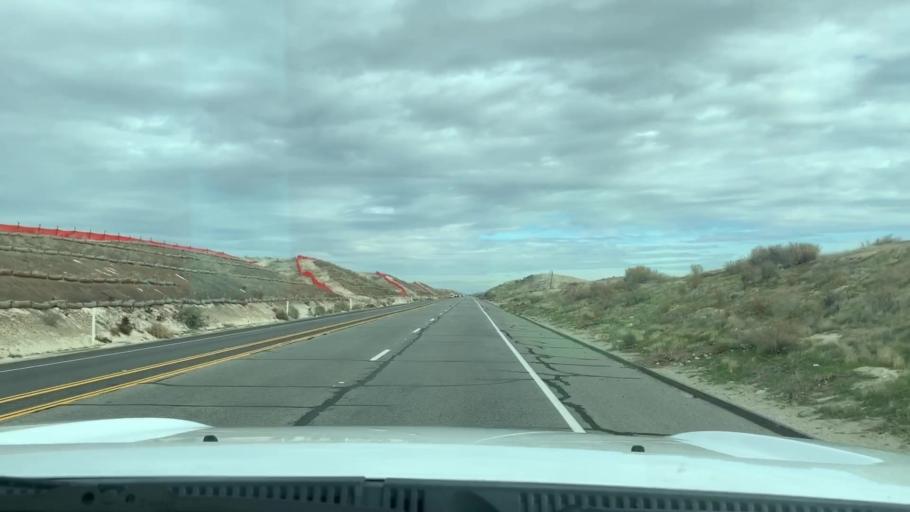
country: US
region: California
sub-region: Kern County
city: Ford City
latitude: 35.2406
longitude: -119.3567
